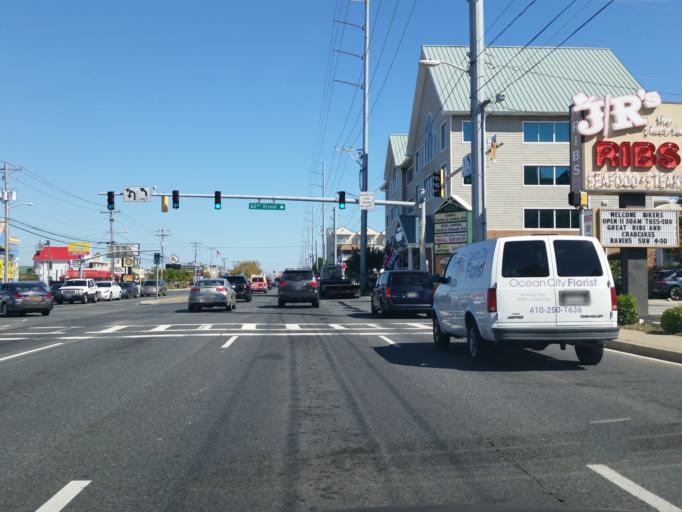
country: US
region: Maryland
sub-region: Worcester County
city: Ocean City
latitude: 38.3848
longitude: -75.0664
